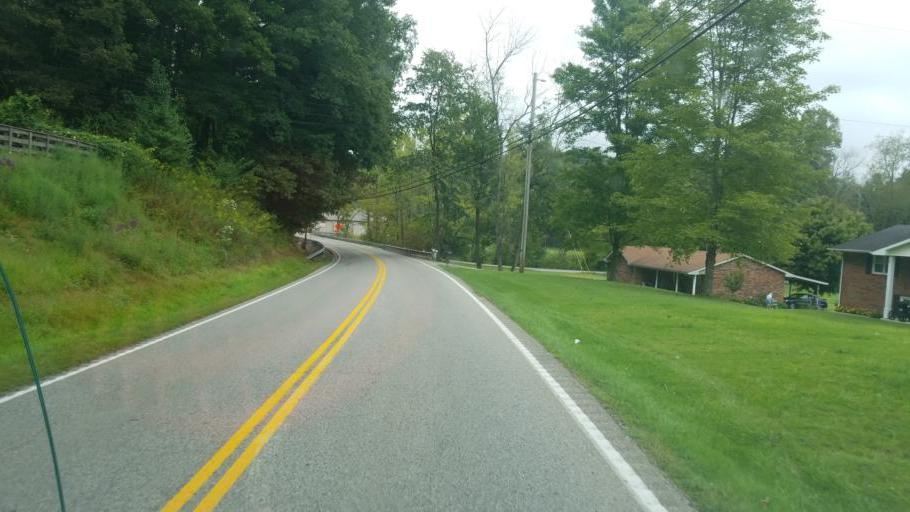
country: US
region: Kentucky
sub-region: Rowan County
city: Morehead
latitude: 38.2081
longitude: -83.4695
